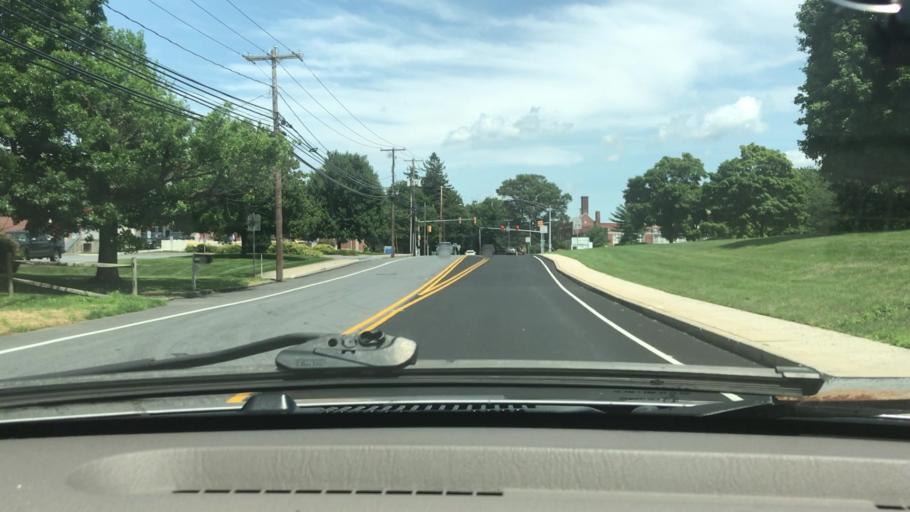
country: US
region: Pennsylvania
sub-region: Dauphin County
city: Paxtonia
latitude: 40.3189
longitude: -76.7897
